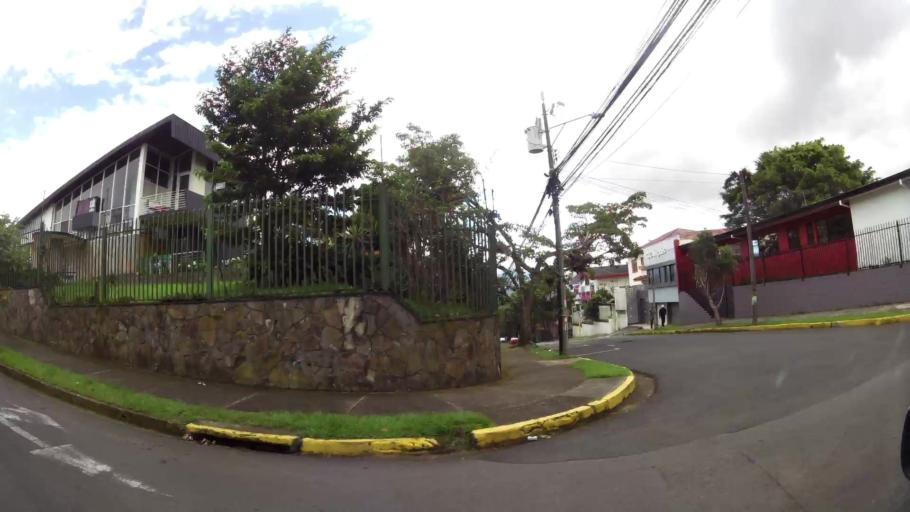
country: CR
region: San Jose
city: San Pedro
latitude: 9.9306
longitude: -84.0609
